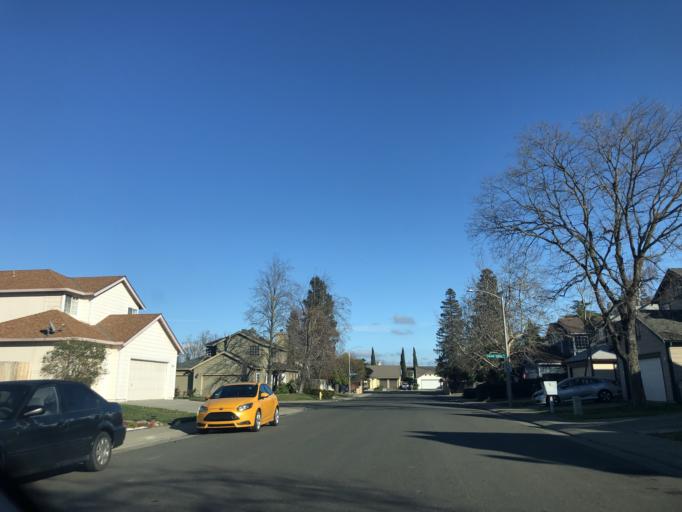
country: US
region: California
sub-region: Yolo County
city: Woodland
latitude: 38.6654
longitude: -121.7488
